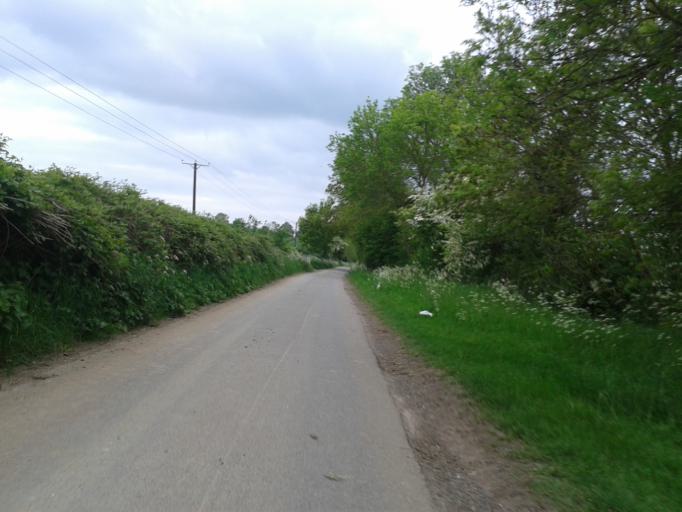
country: GB
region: England
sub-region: Leicestershire
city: Cosby
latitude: 52.5299
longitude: -1.1912
